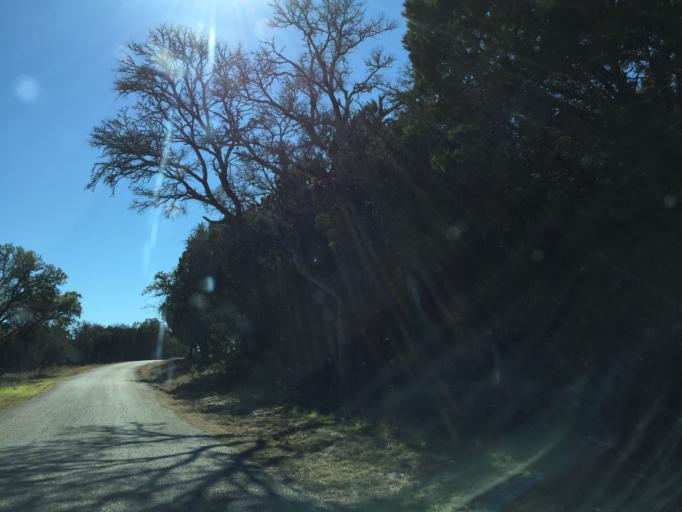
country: US
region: Texas
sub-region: Burnet County
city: Bertram
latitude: 30.9051
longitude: -98.1025
